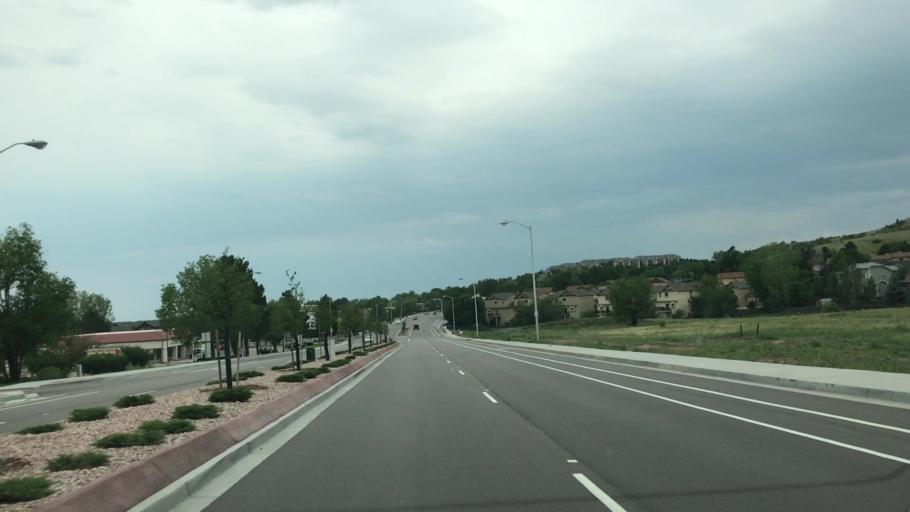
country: US
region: Colorado
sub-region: El Paso County
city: Colorado Springs
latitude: 38.8927
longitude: -104.8510
